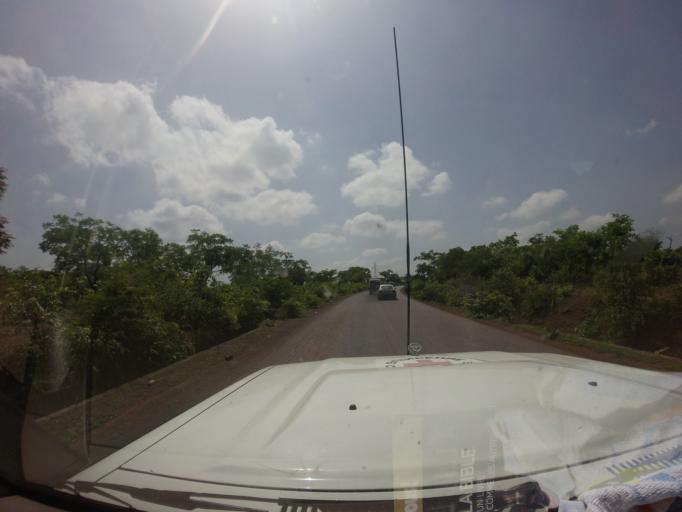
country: GN
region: Mamou
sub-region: Mamou Prefecture
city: Mamou
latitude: 10.2928
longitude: -12.3542
